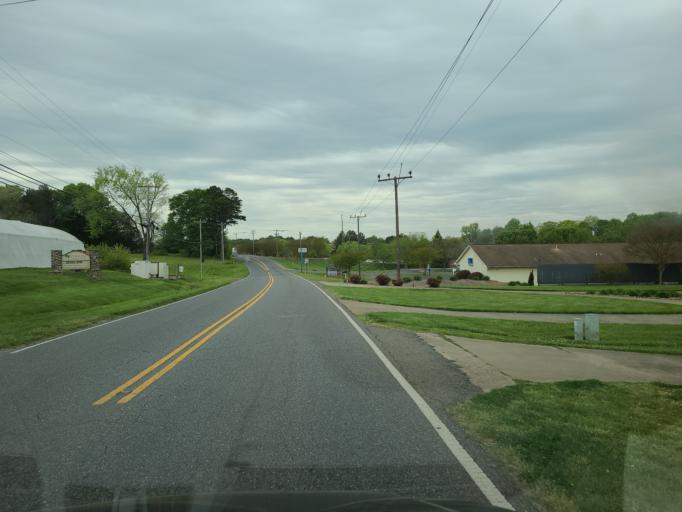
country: US
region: North Carolina
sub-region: Cleveland County
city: Shelby
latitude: 35.3046
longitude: -81.5040
